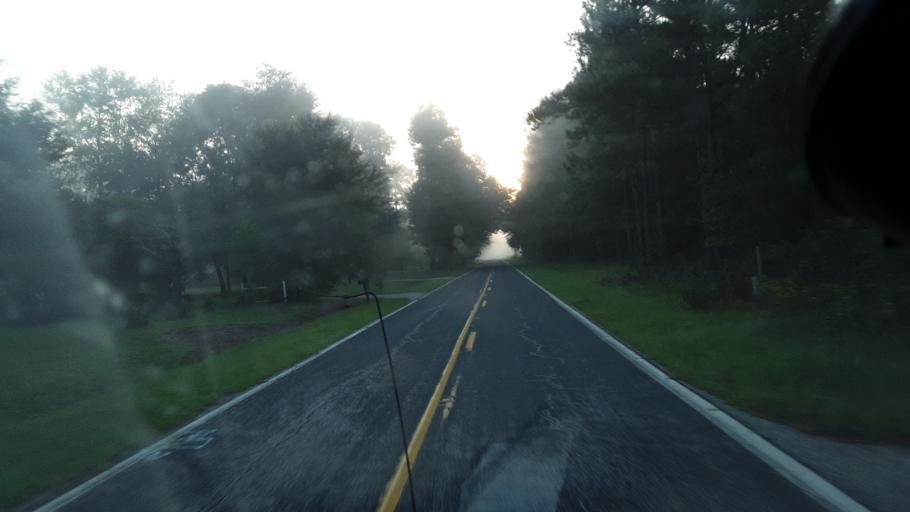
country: US
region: South Carolina
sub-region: Clarendon County
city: Manning
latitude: 33.7295
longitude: -80.1051
